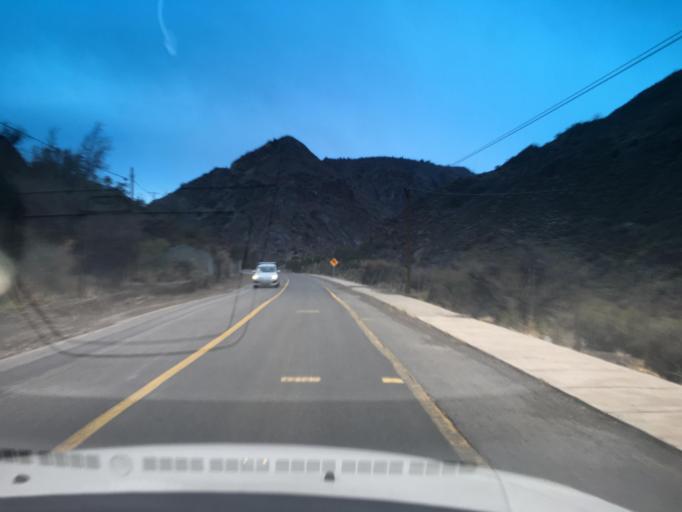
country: CL
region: Santiago Metropolitan
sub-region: Provincia de Cordillera
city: Puente Alto
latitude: -33.7384
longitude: -70.2985
